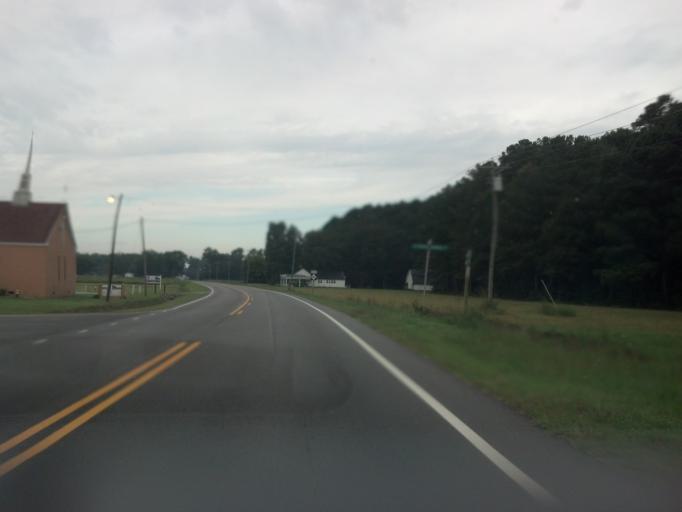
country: US
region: North Carolina
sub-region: Greene County
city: Maury
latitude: 35.4694
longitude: -77.5262
